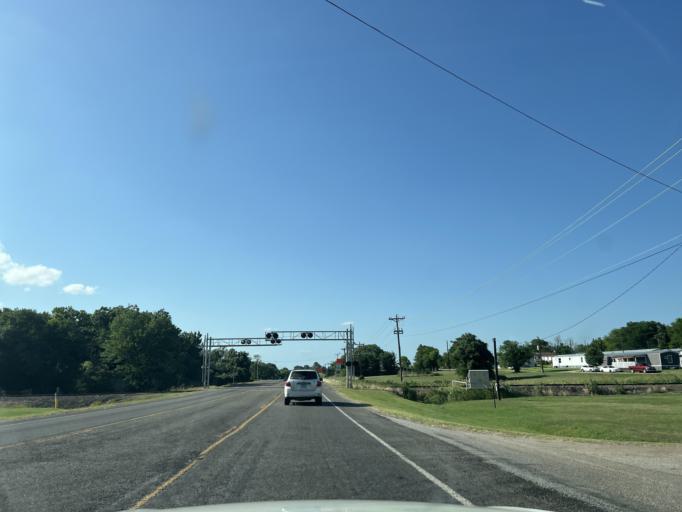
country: US
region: Texas
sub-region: Washington County
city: Brenham
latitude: 30.1661
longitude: -96.3808
